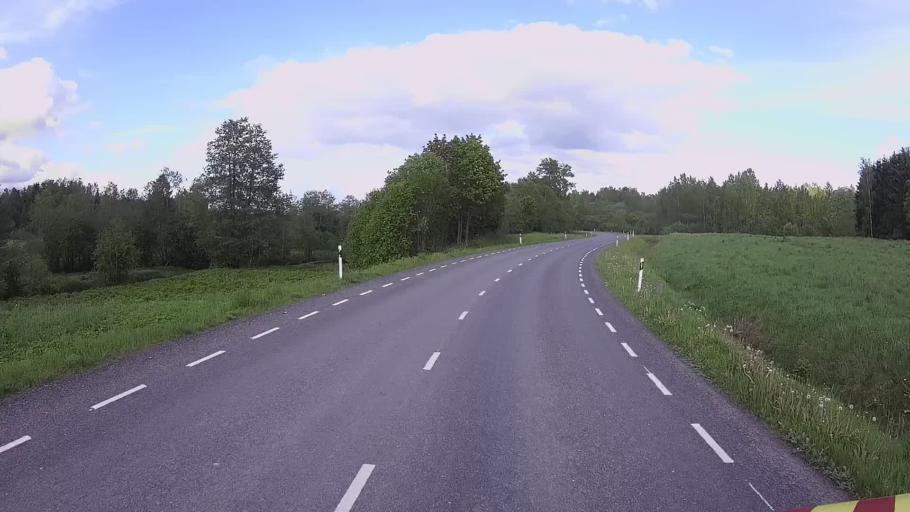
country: EE
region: Jogevamaa
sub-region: Mustvee linn
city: Mustvee
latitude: 58.9815
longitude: 26.8339
